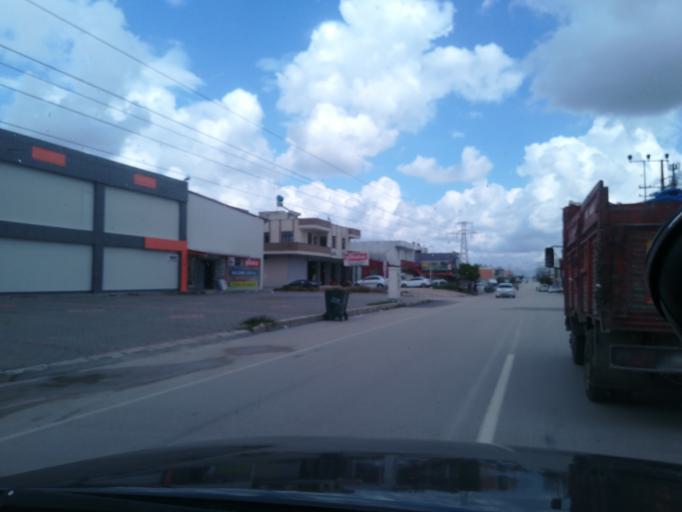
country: TR
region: Adana
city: Yuregir
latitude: 36.9765
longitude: 35.3871
